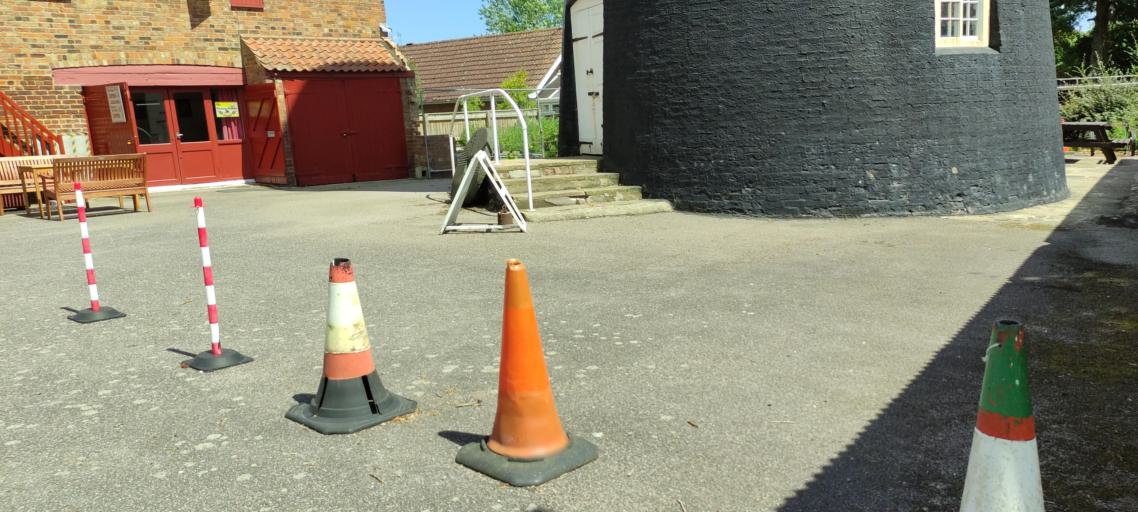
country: GB
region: England
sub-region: Lincolnshire
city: Burgh le Marsh
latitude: 53.1607
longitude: 0.2476
